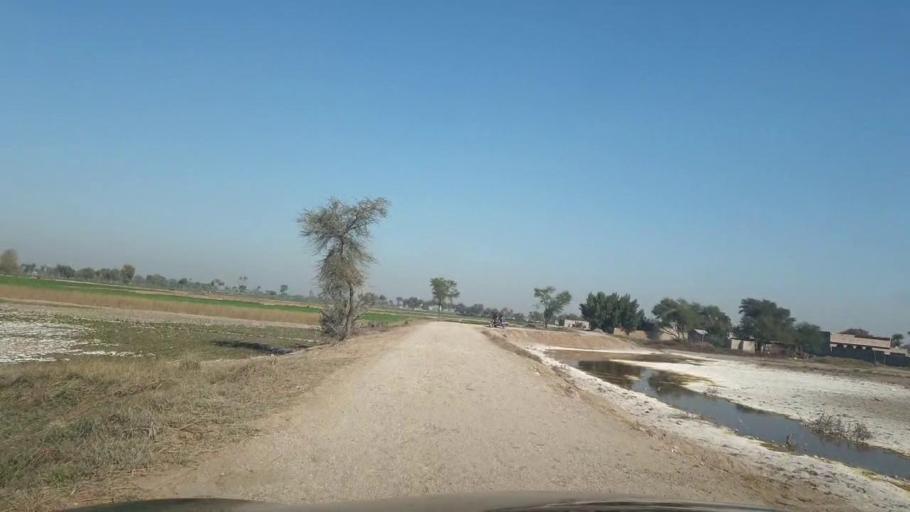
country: PK
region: Sindh
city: Ghotki
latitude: 27.9982
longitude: 69.3562
